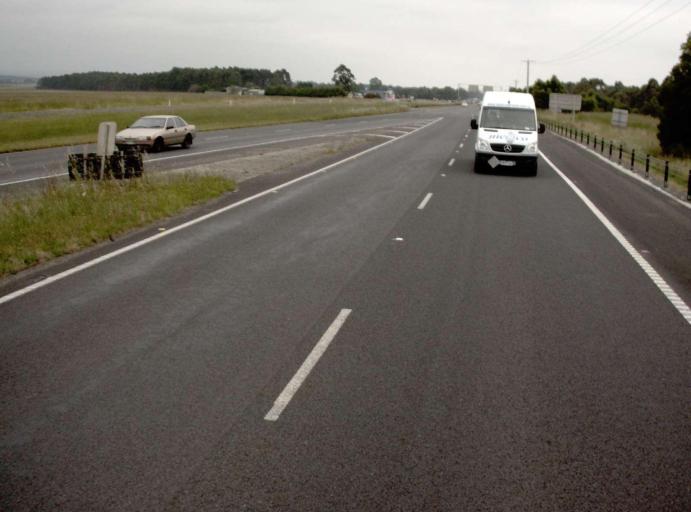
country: AU
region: Victoria
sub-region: Latrobe
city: Morwell
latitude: -38.2278
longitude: 146.4616
